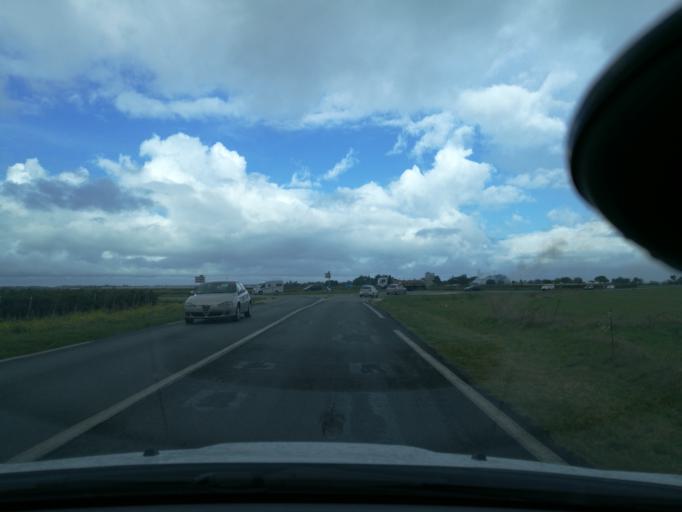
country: FR
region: Poitou-Charentes
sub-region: Departement de la Charente-Maritime
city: Saint-Martin-de-Re
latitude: 46.1978
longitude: -1.3703
